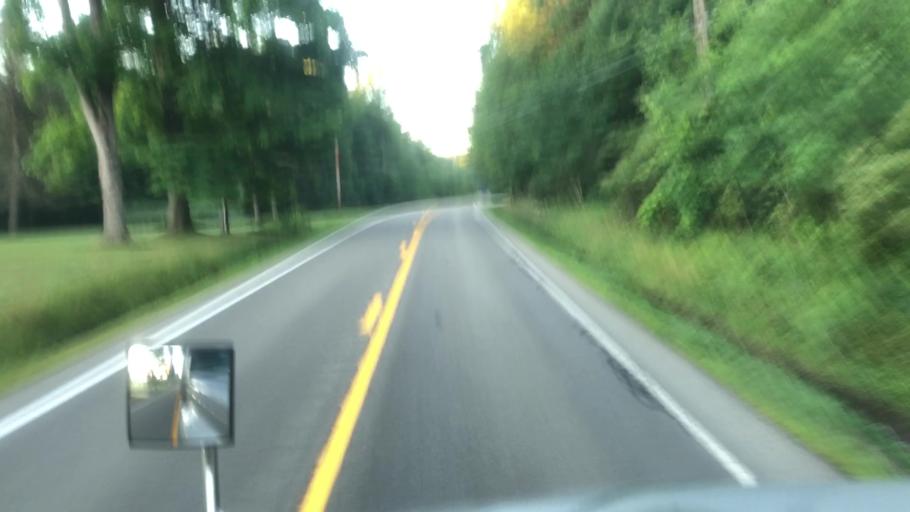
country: US
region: Pennsylvania
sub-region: Crawford County
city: Titusville
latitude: 41.5719
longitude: -79.6100
